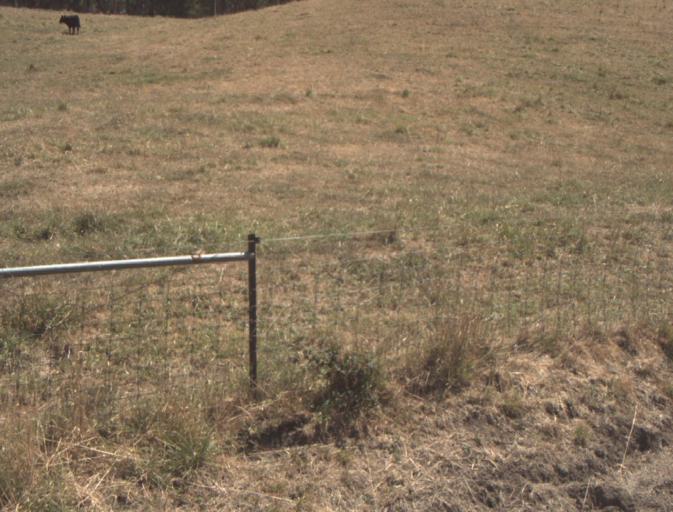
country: AU
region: Tasmania
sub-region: Launceston
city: Mayfield
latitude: -41.2658
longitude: 147.1285
